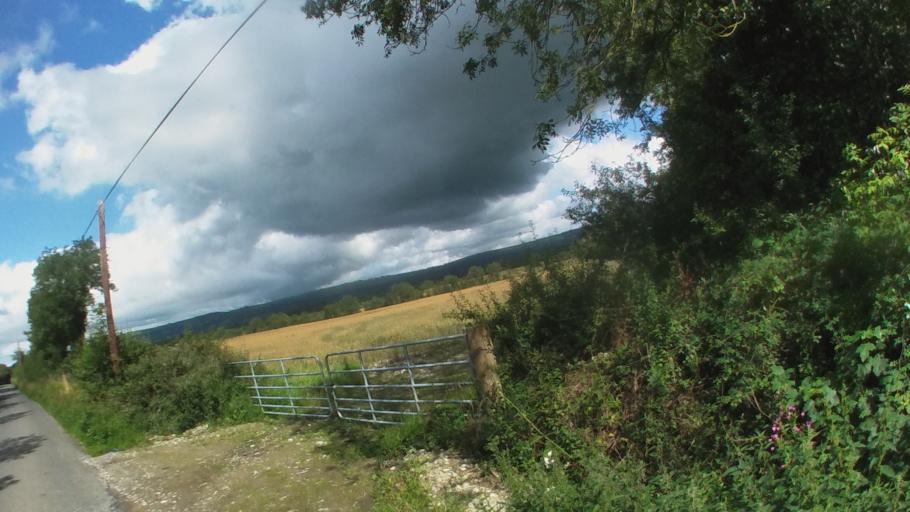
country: IE
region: Leinster
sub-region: Kilkenny
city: Kilkenny
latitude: 52.6809
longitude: -7.2212
